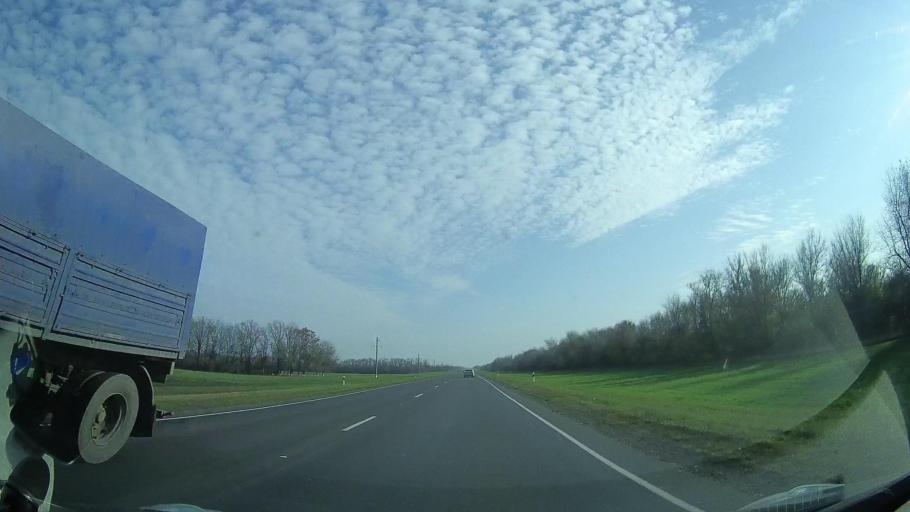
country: RU
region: Rostov
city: Gigant
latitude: 46.5282
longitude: 41.2024
